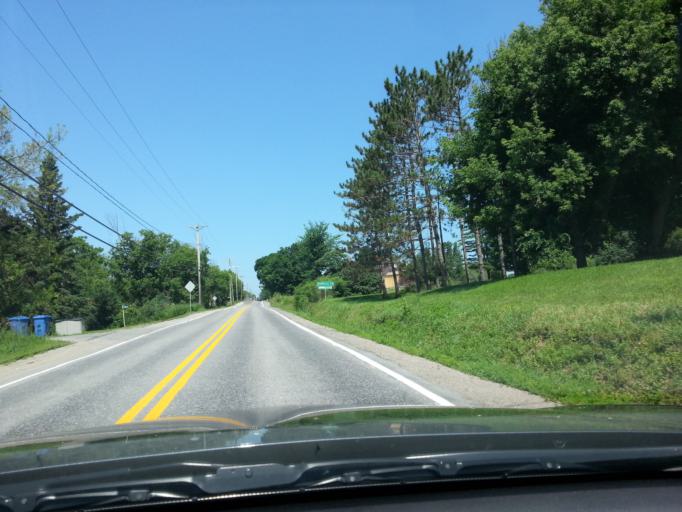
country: CA
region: Ontario
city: Bells Corners
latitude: 45.4321
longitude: -75.9038
